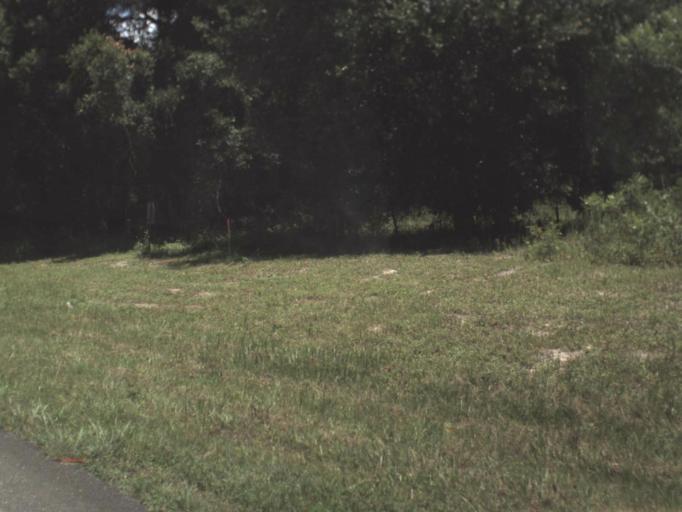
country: US
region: Florida
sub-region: Clay County
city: Keystone Heights
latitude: 29.7538
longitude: -82.0567
